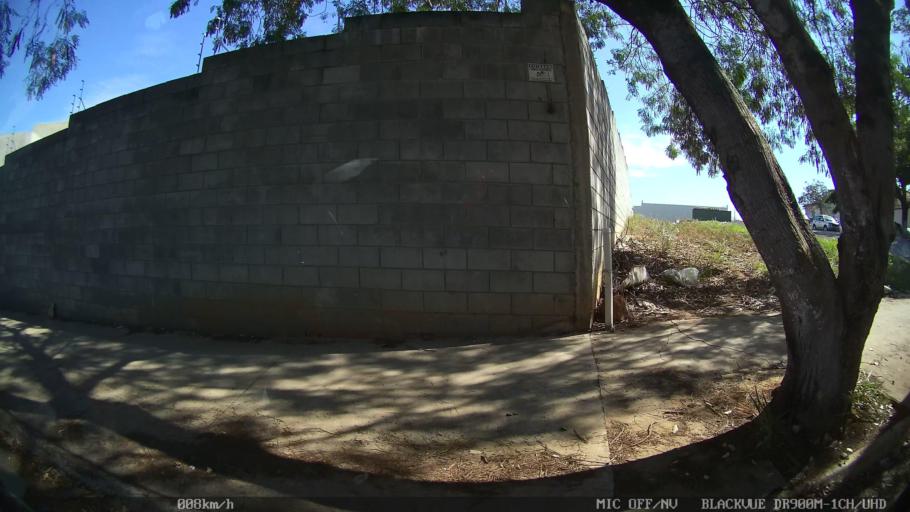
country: BR
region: Sao Paulo
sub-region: Santa Barbara D'Oeste
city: Santa Barbara d'Oeste
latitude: -22.7401
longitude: -47.4097
